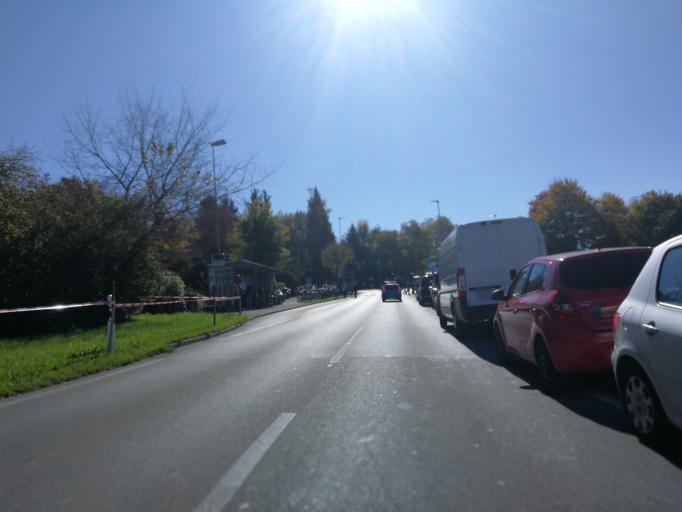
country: CH
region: Zurich
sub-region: Bezirk Hinwil
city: Binzikon
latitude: 47.2842
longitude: 8.7664
